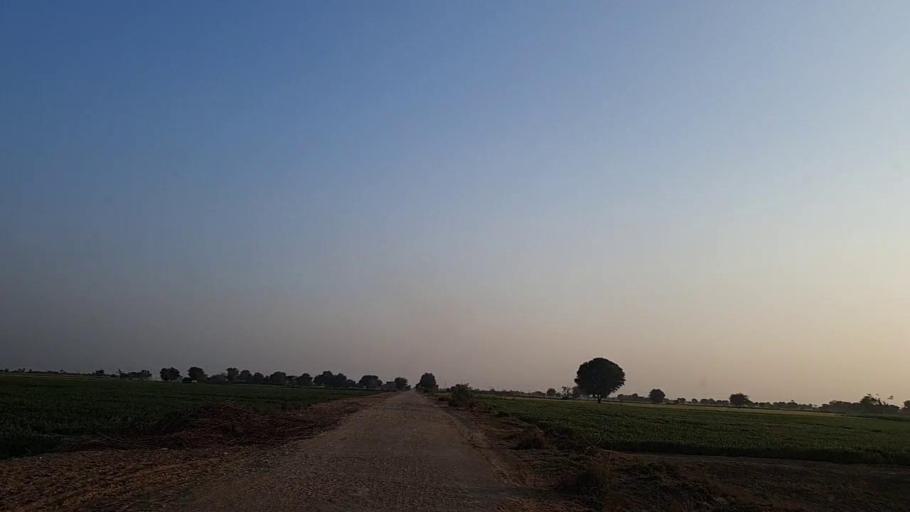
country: PK
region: Sindh
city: Shahdadpur
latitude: 26.0037
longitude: 68.4923
